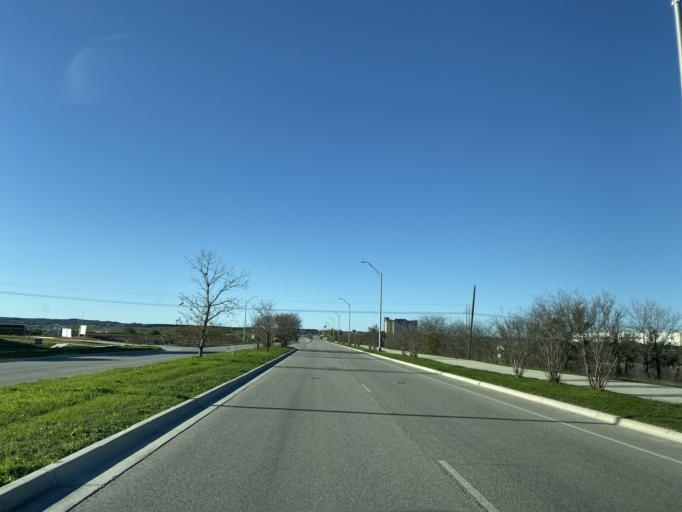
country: US
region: Texas
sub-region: Guadalupe County
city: Redwood
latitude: 29.8311
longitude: -97.9624
